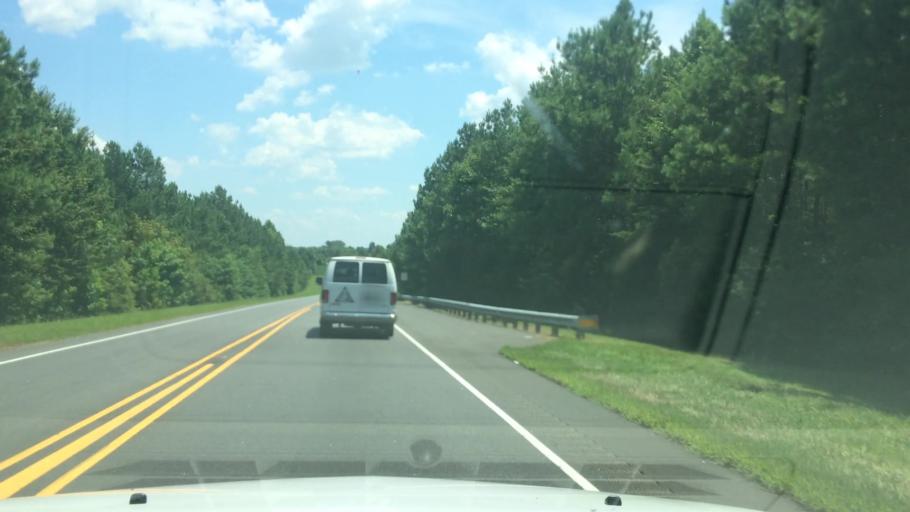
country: US
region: North Carolina
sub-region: Iredell County
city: Statesville
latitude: 35.8078
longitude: -80.9693
